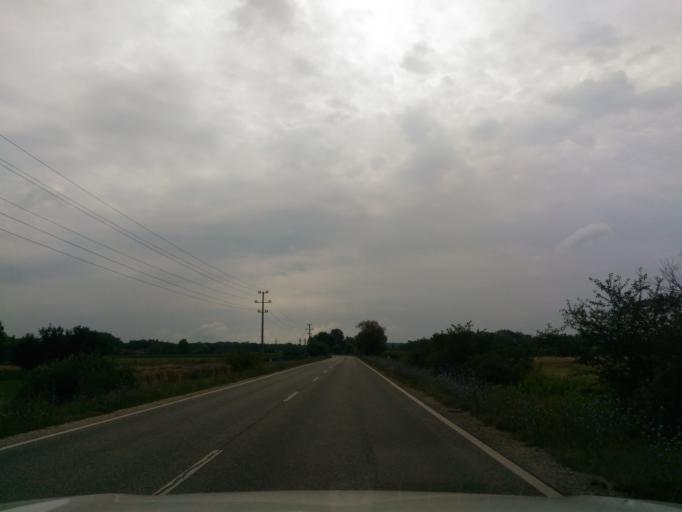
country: HU
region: Pest
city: Ujhartyan
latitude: 47.2131
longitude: 19.3852
